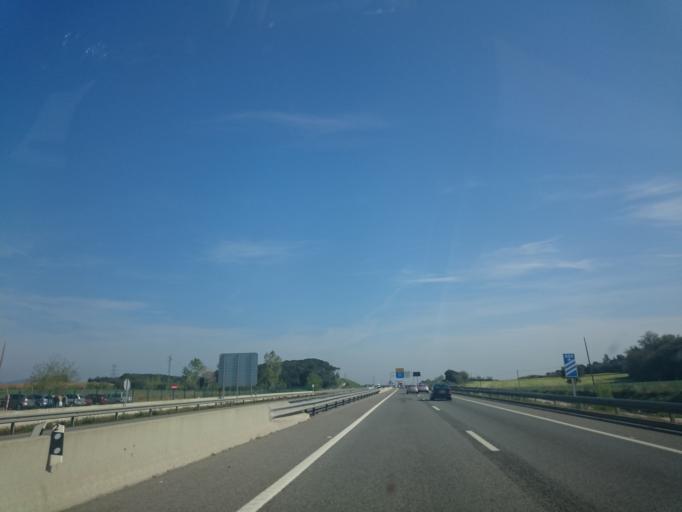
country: ES
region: Catalonia
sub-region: Provincia de Girona
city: Fornells de la Selva
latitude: 41.9177
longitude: 2.7921
